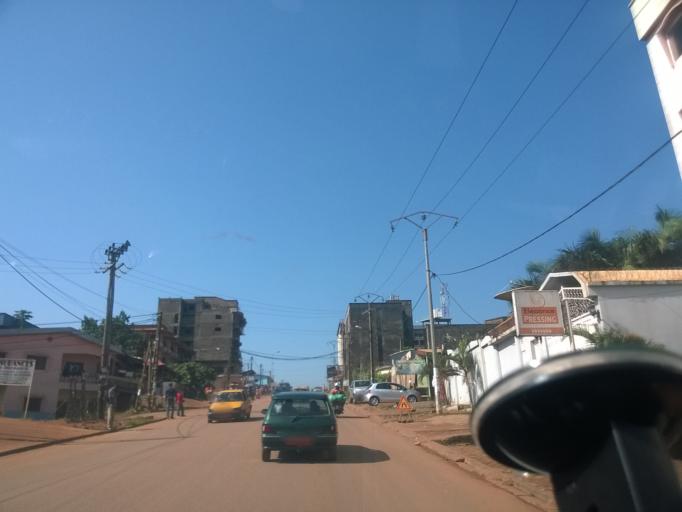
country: CM
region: Centre
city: Yaounde
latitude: 3.8299
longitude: 11.4811
